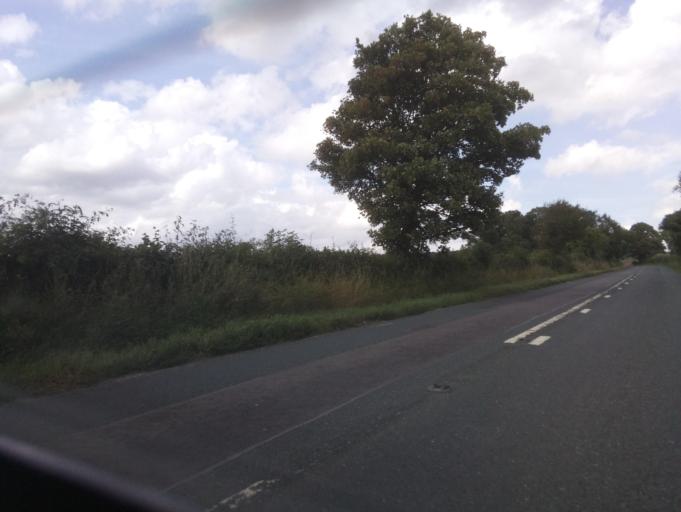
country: GB
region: England
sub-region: North Yorkshire
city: Catterick Garrison
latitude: 54.4276
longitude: -1.6819
